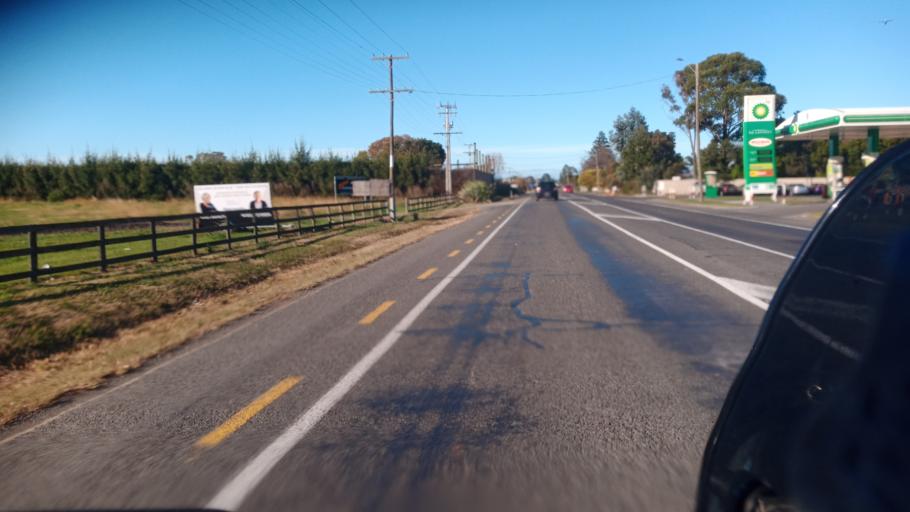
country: NZ
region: Hawke's Bay
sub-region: Napier City
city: Napier
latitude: -39.4248
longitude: 176.8697
